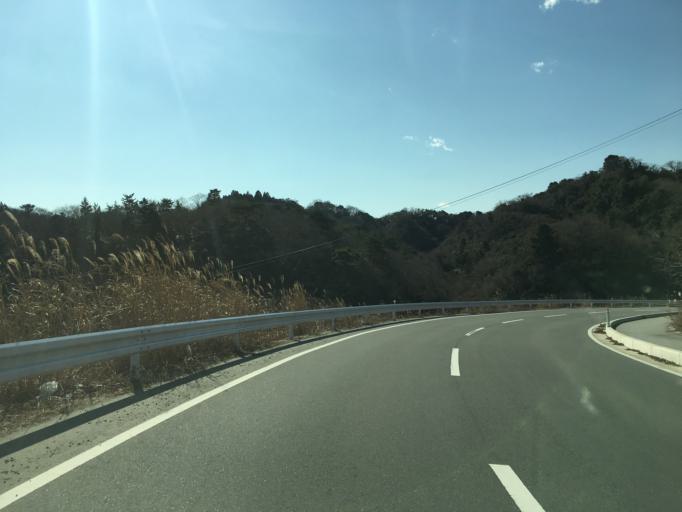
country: JP
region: Fukushima
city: Iwaki
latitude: 37.1205
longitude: 140.9920
